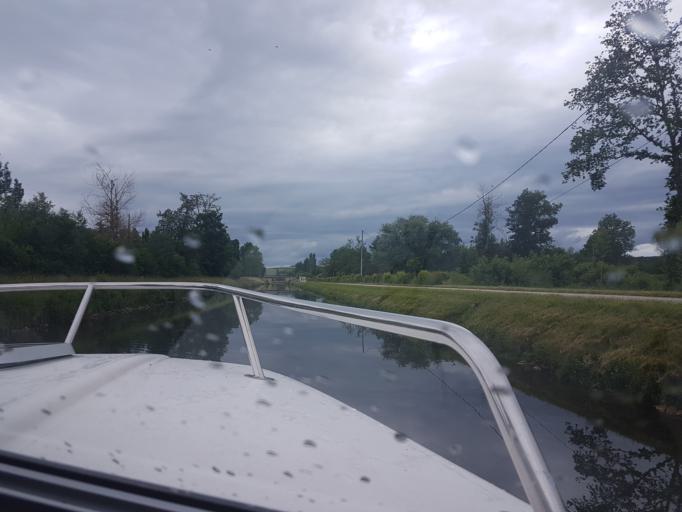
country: FR
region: Bourgogne
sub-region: Departement de l'Yonne
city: Saint-Bris-le-Vineux
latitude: 47.7090
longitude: 3.6364
